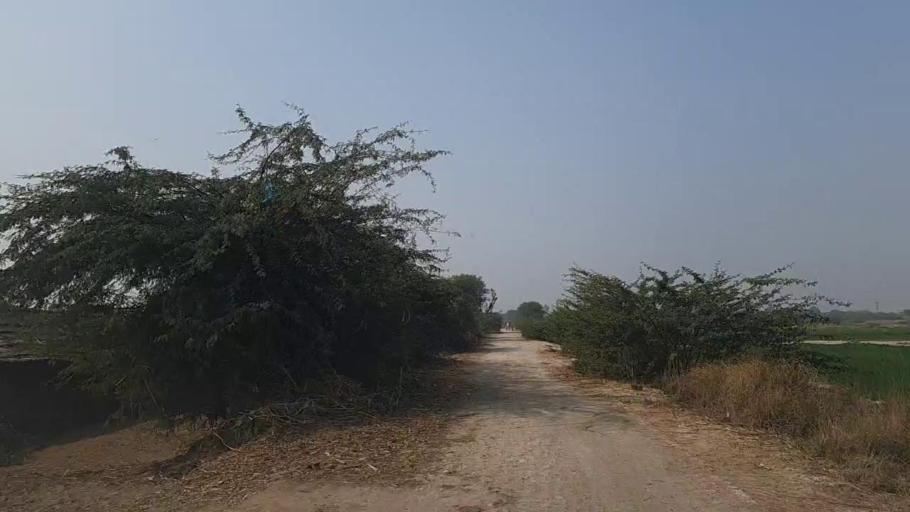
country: PK
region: Sindh
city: Daur
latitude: 26.4267
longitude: 68.4495
